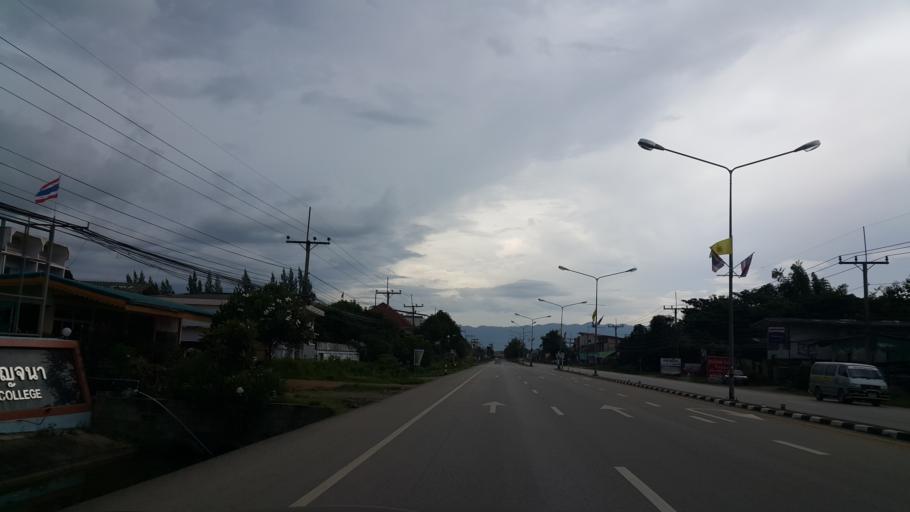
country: TH
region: Phayao
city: Dok Kham Tai
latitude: 19.1616
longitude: 99.9767
